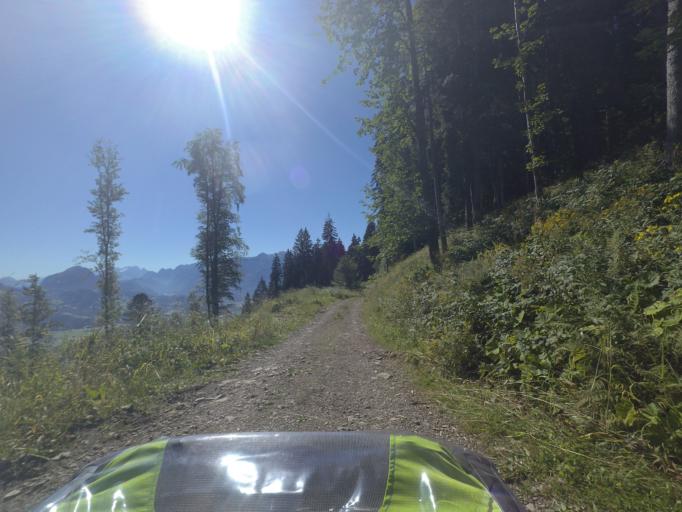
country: AT
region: Salzburg
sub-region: Politischer Bezirk Hallein
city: Kuchl
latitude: 47.6370
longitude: 13.1027
